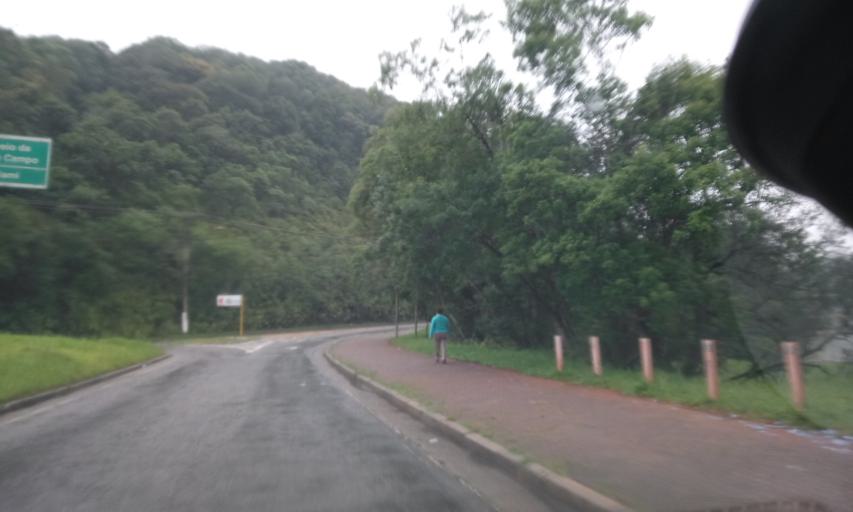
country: BR
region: Sao Paulo
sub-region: Maua
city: Maua
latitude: -23.7247
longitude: -46.4951
